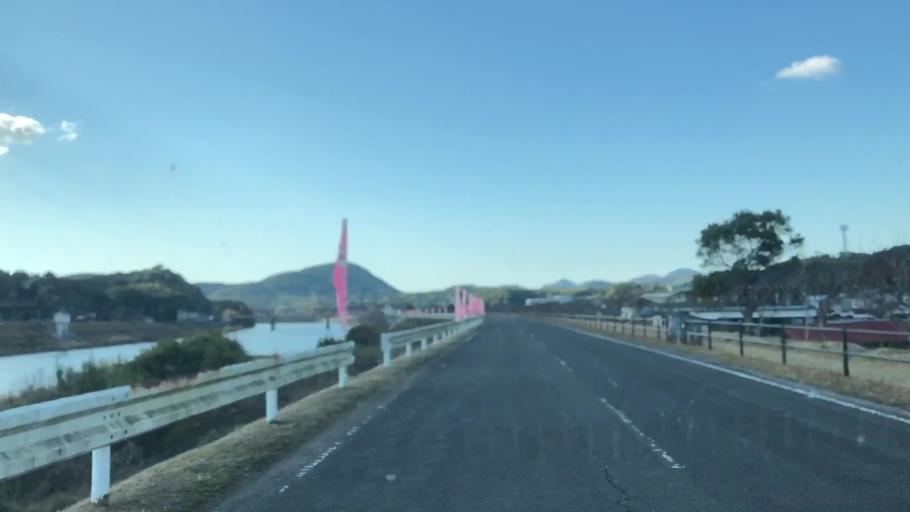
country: JP
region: Kagoshima
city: Satsumasendai
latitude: 31.8600
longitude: 130.3449
